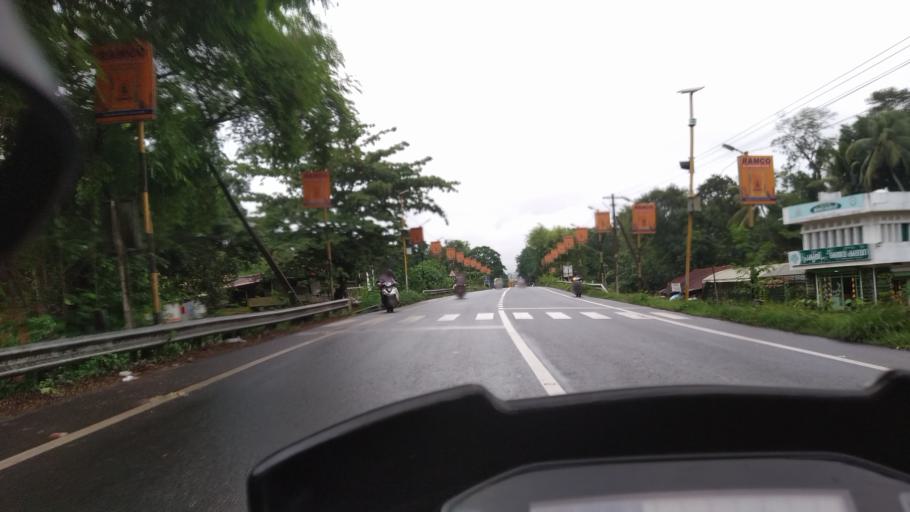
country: IN
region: Kerala
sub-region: Alappuzha
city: Mavelikara
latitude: 9.2816
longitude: 76.4452
